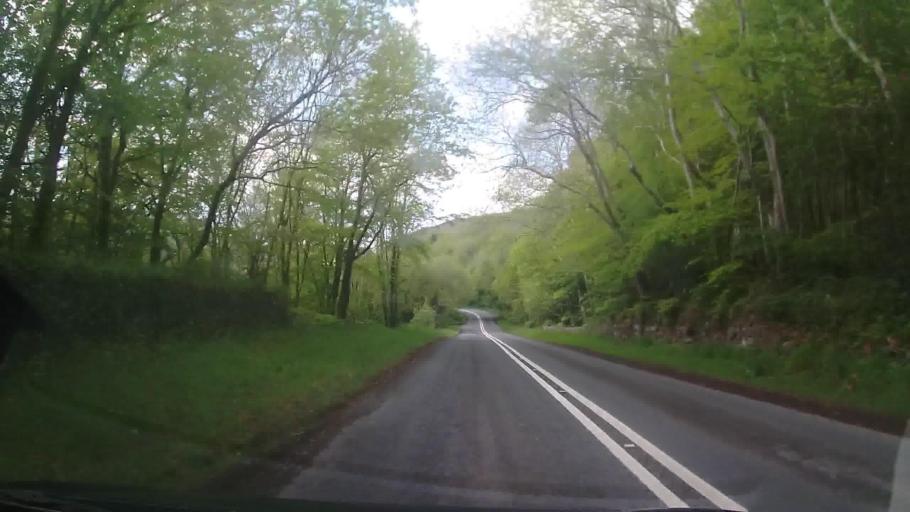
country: GB
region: Wales
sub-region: Gwynedd
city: Porthmadog
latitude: 52.9427
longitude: -4.1304
